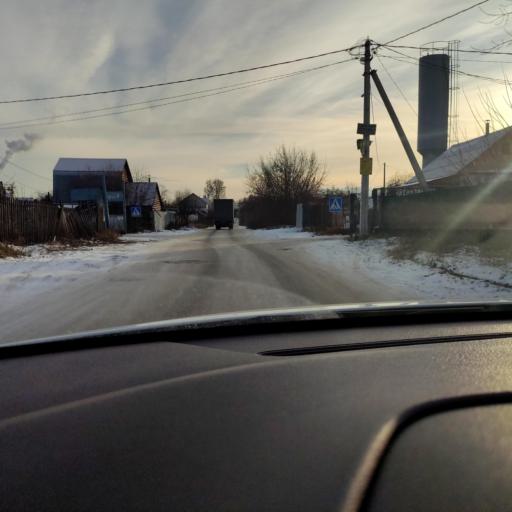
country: RU
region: Tatarstan
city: Staroye Arakchino
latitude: 55.8641
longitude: 49.0468
